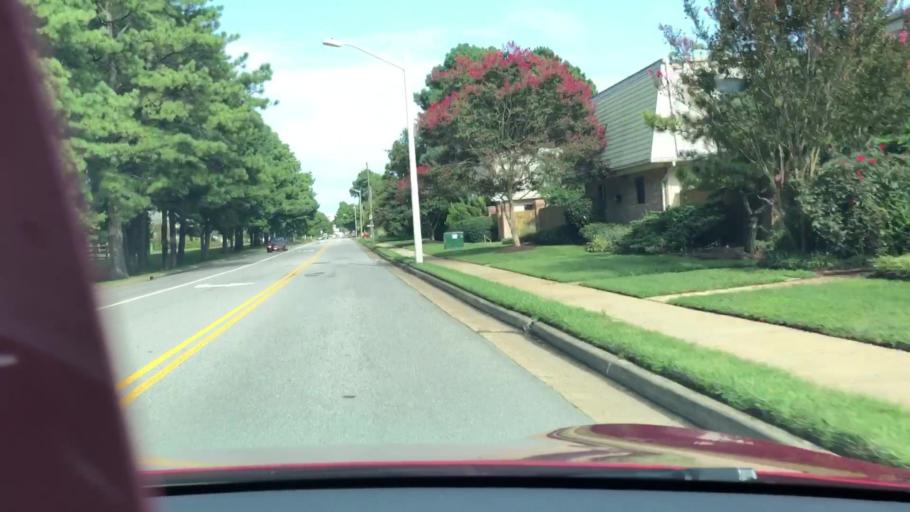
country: US
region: Virginia
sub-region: City of Virginia Beach
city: Virginia Beach
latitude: 36.8378
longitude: -75.9896
